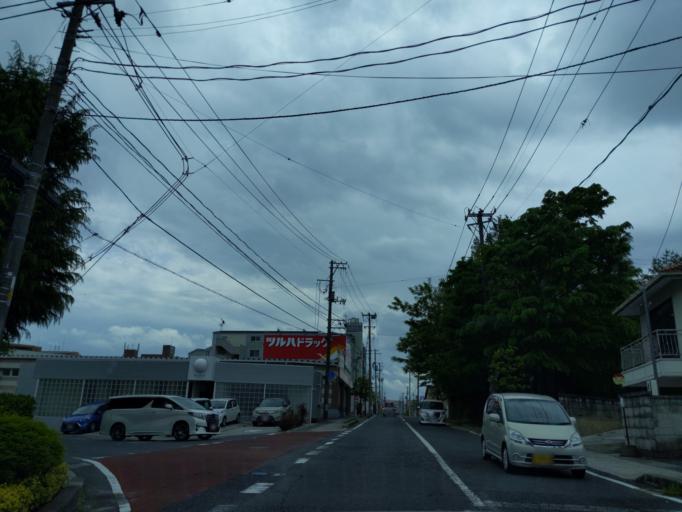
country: JP
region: Fukushima
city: Koriyama
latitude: 37.3915
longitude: 140.3720
